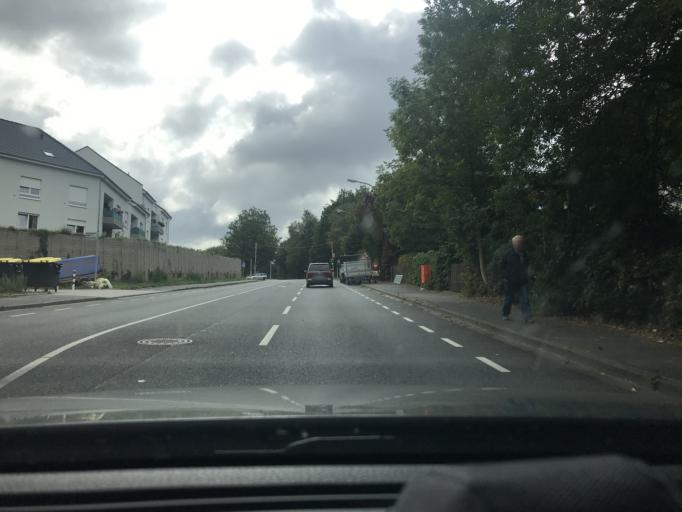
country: DE
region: North Rhine-Westphalia
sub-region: Regierungsbezirk Dusseldorf
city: Mettmann
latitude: 51.2453
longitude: 6.9760
